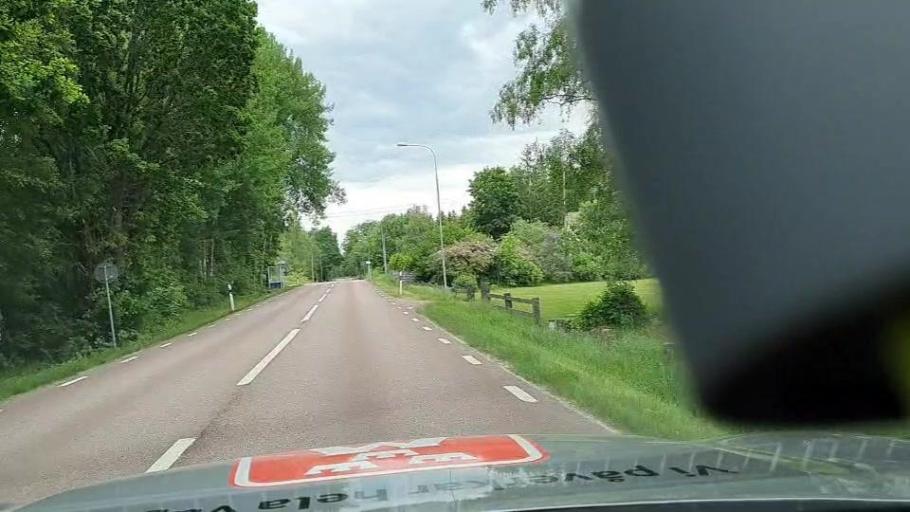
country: SE
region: Kalmar
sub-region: Emmaboda Kommun
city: Emmaboda
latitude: 56.4595
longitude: 15.5892
